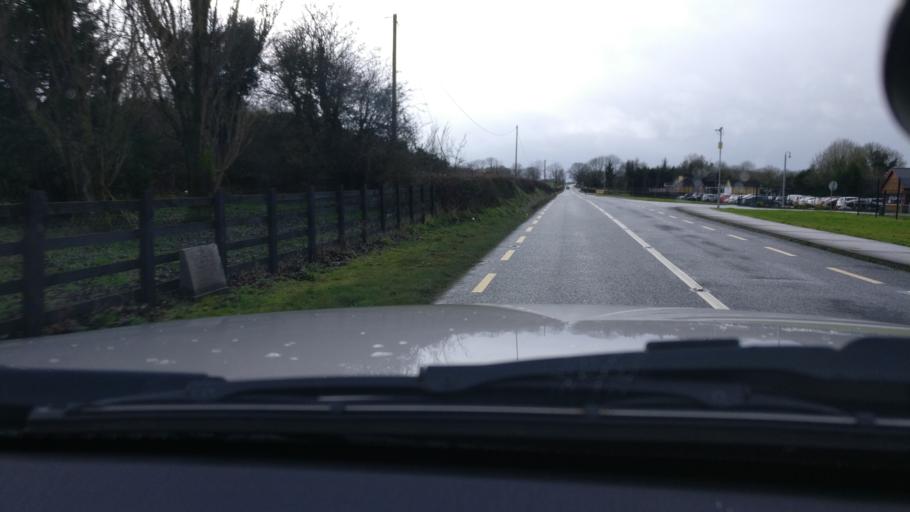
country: IE
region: Leinster
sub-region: An Longfort
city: Ballymahon
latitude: 53.5529
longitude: -7.7725
